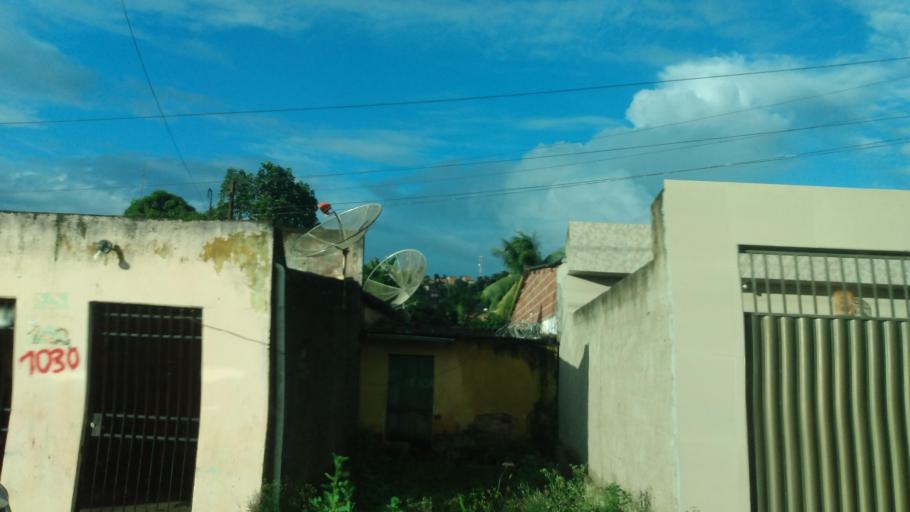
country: BR
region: Pernambuco
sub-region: Palmares
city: Palmares
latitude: -8.6790
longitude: -35.5968
